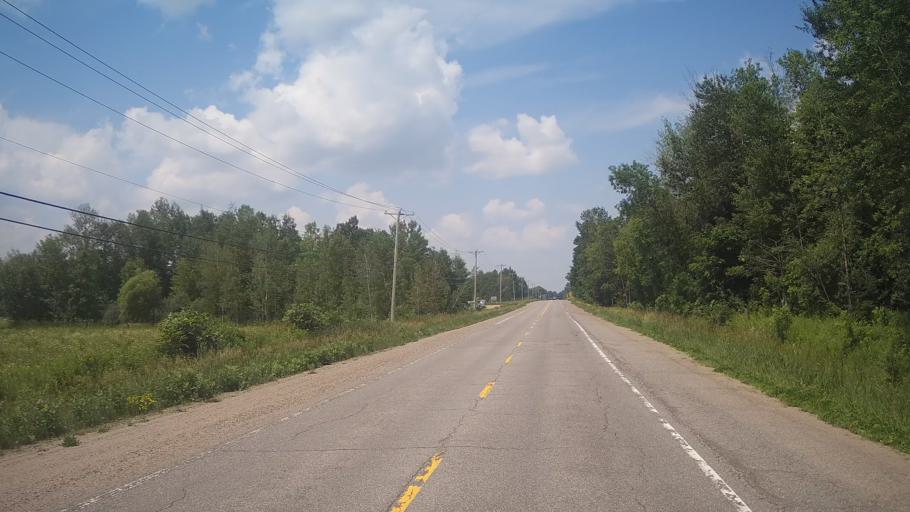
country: CA
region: Quebec
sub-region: Outaouais
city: Shawville
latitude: 45.5700
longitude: -76.4345
